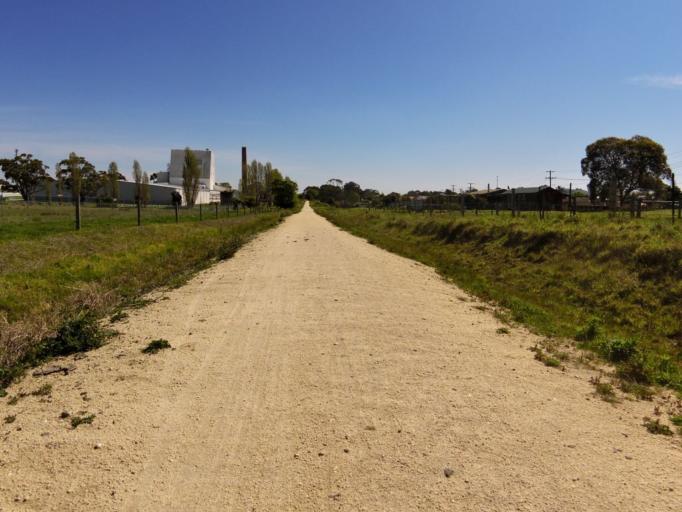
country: AU
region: Victoria
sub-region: Latrobe
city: Morwell
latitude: -38.6676
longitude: 146.3309
